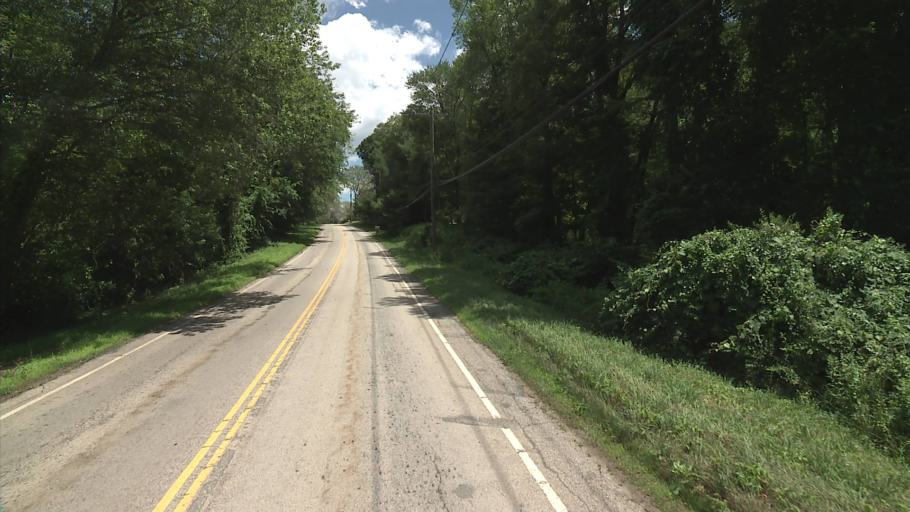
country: US
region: Connecticut
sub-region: Middlesex County
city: East Haddam
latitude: 41.4633
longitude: -72.4406
